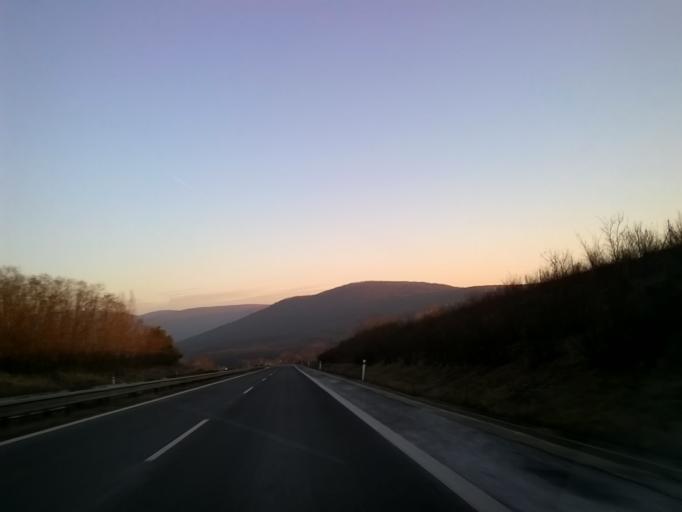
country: SK
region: Nitriansky
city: Tlmace
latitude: 48.3678
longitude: 18.5448
